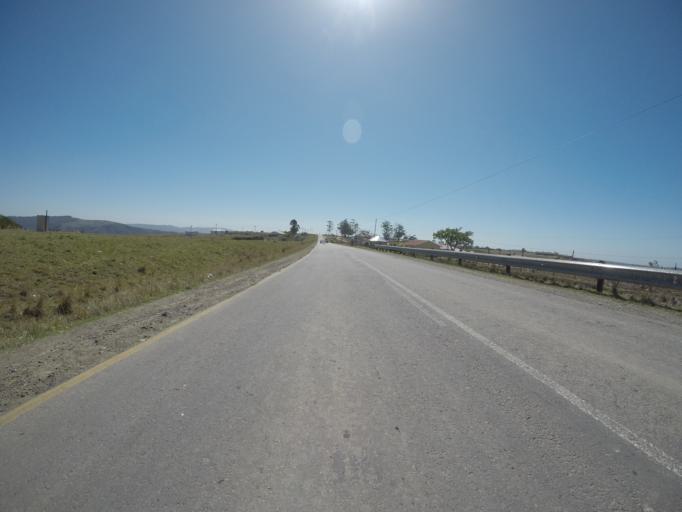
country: ZA
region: Eastern Cape
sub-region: OR Tambo District Municipality
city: Libode
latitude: -31.9203
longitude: 28.9740
